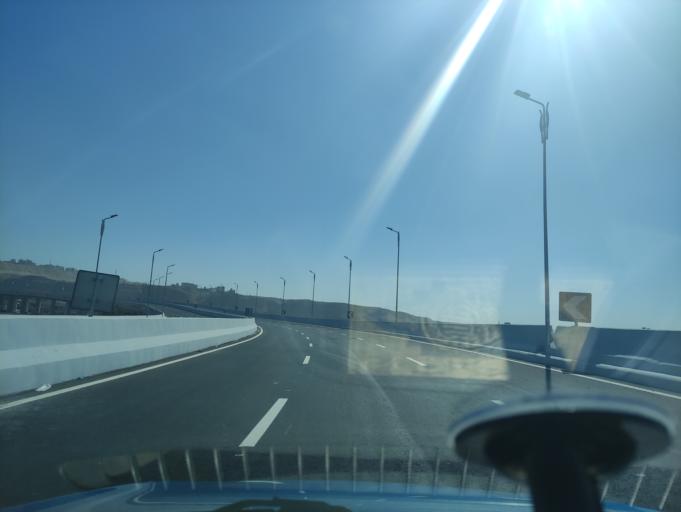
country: EG
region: Al Jizah
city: Al Jizah
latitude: 30.0067
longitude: 31.2638
